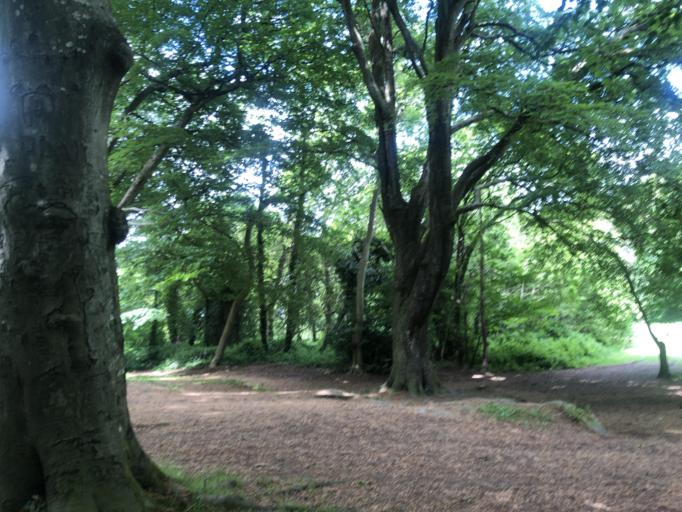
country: IE
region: Leinster
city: Dalkey
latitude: 53.2677
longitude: -6.1103
